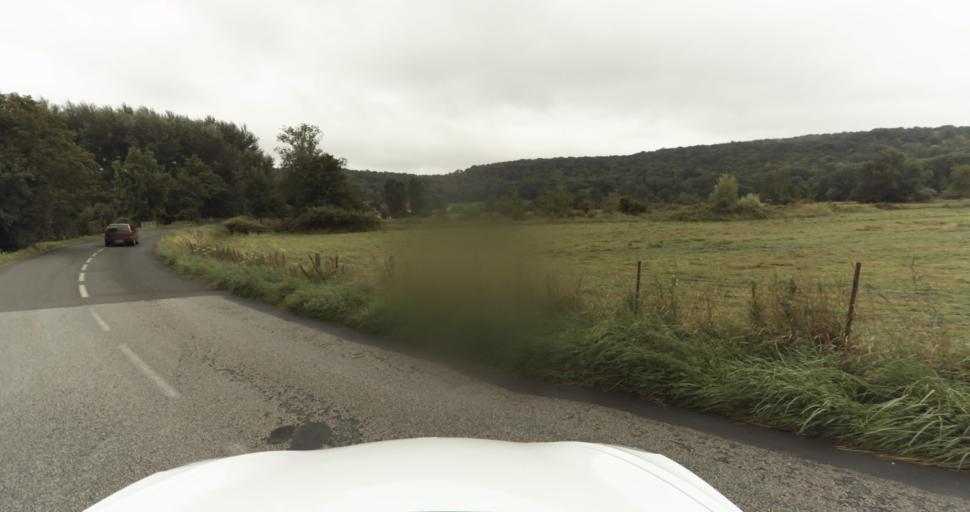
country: FR
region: Haute-Normandie
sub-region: Departement de l'Eure
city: Aviron
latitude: 49.0998
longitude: 1.1137
